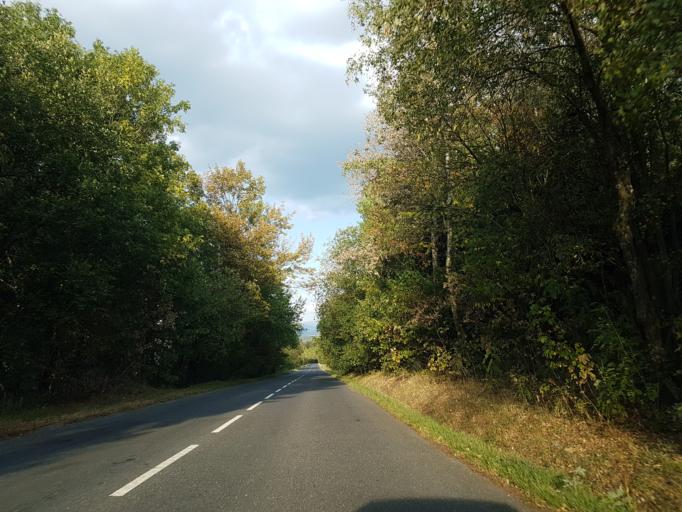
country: CZ
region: Liberecky
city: Mala Skala
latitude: 50.6649
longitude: 15.1703
